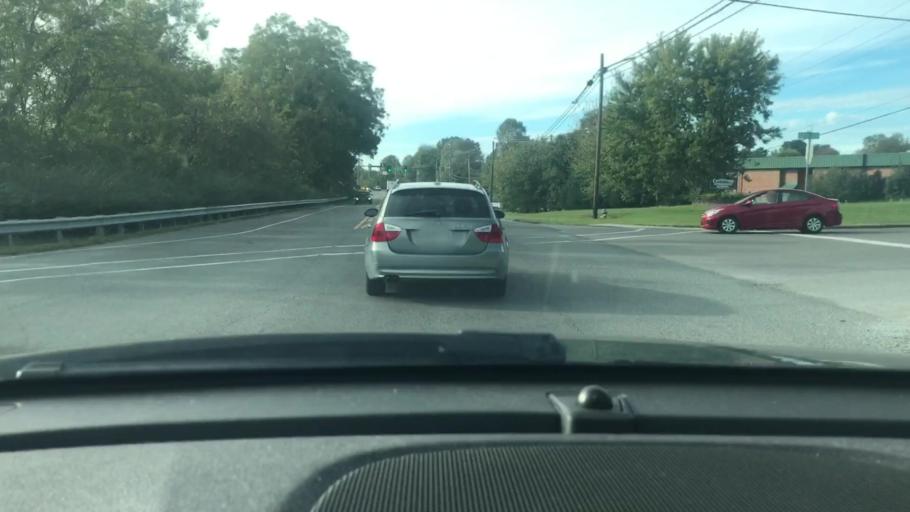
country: US
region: Tennessee
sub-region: Williamson County
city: Franklin
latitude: 35.9260
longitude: -86.8843
